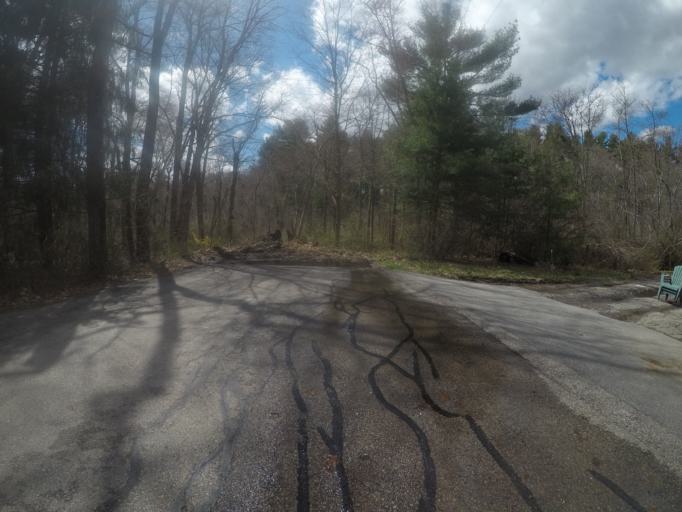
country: US
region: Massachusetts
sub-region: Bristol County
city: Easton
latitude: 42.0295
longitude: -71.0751
